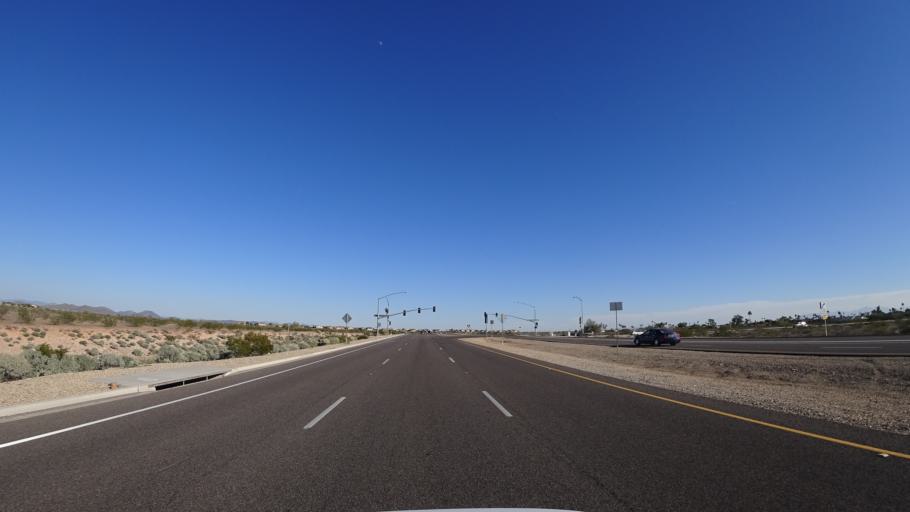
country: US
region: Arizona
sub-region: Maricopa County
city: Sun City West
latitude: 33.6850
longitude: -112.3299
